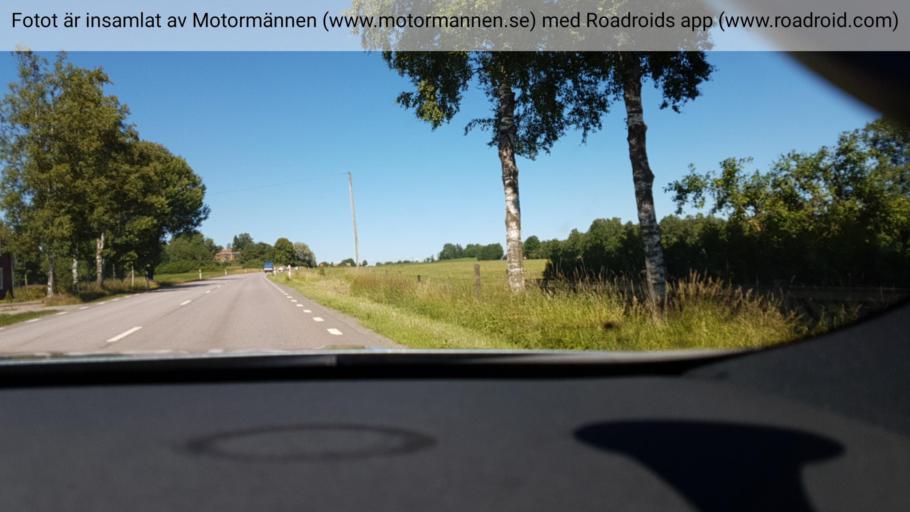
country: SE
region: Vaestra Goetaland
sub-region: Falkopings Kommun
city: Falkoeping
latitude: 58.0968
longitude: 13.5272
